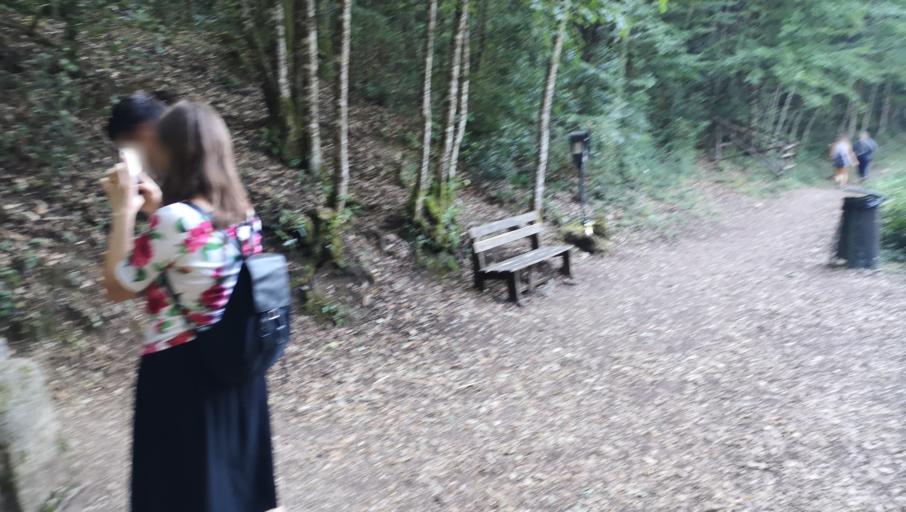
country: IT
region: Umbria
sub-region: Provincia di Terni
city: Narni
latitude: 42.5070
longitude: 12.5387
